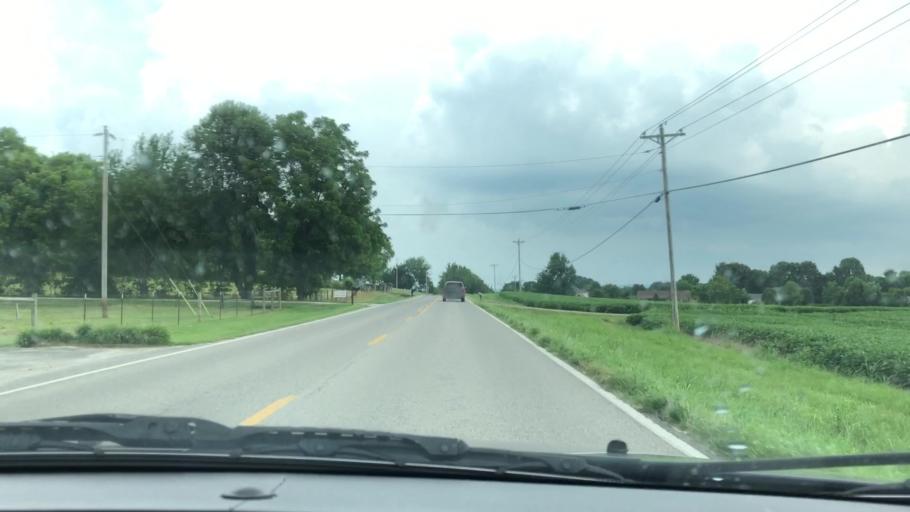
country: US
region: Tennessee
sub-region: Maury County
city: Spring Hill
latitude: 35.7144
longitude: -87.0145
